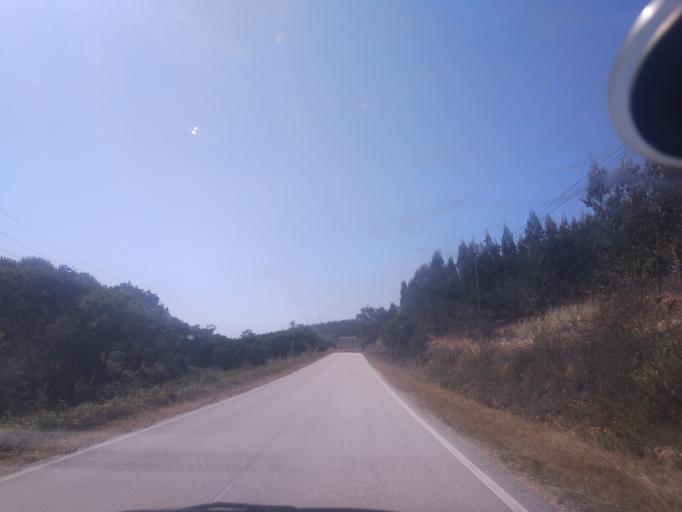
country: PT
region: Faro
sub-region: Aljezur
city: Aljezur
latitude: 37.2174
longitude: -8.7895
